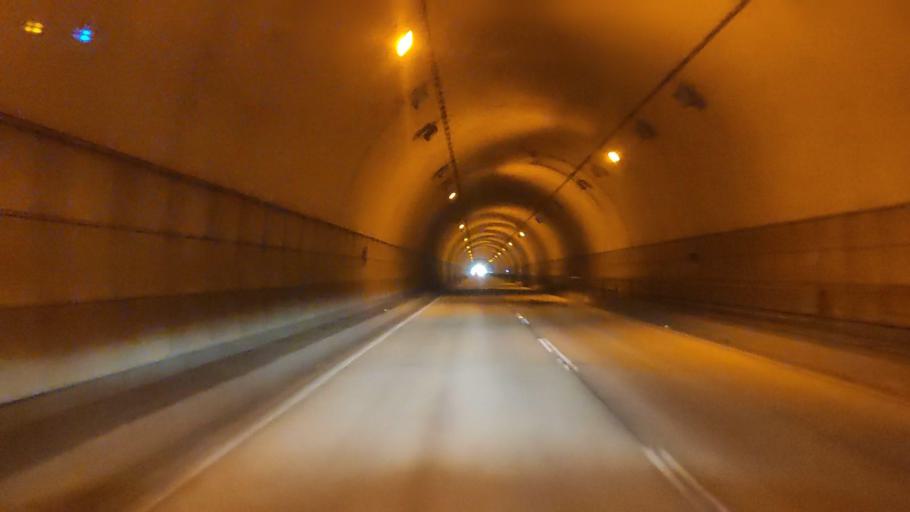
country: JP
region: Miyazaki
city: Nobeoka
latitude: 32.6713
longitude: 131.7687
